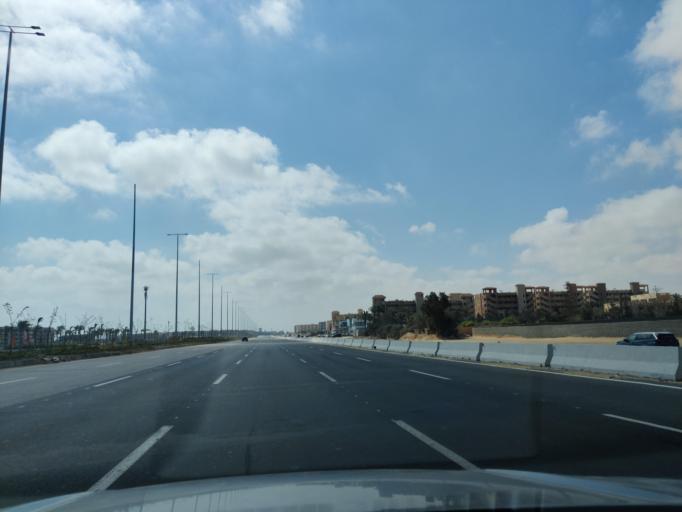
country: EG
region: Muhafazat Matruh
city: Al `Alamayn
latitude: 30.9620
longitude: 28.7554
